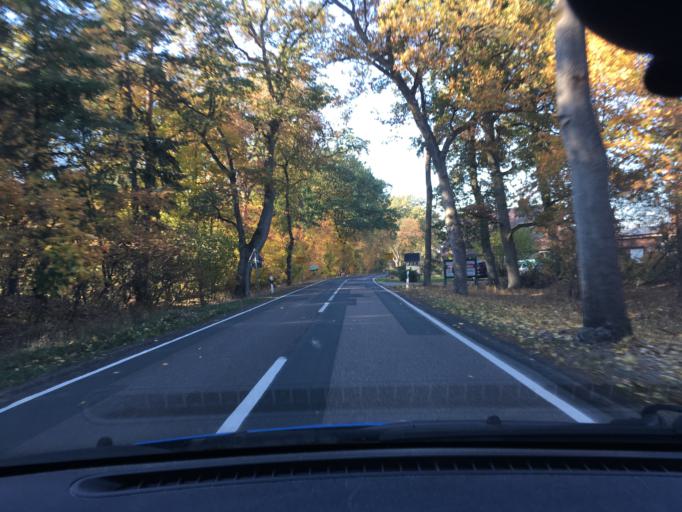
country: DE
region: Lower Saxony
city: Damnatz
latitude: 53.1681
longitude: 11.1709
